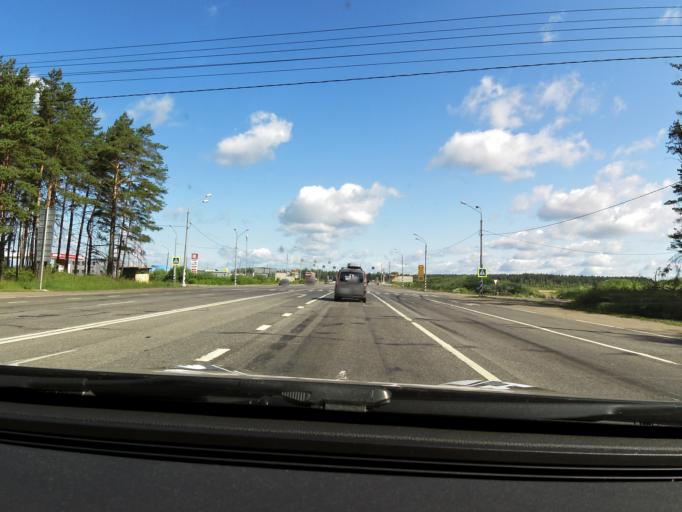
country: RU
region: Tverskaya
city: Tver
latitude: 56.8761
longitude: 35.7849
